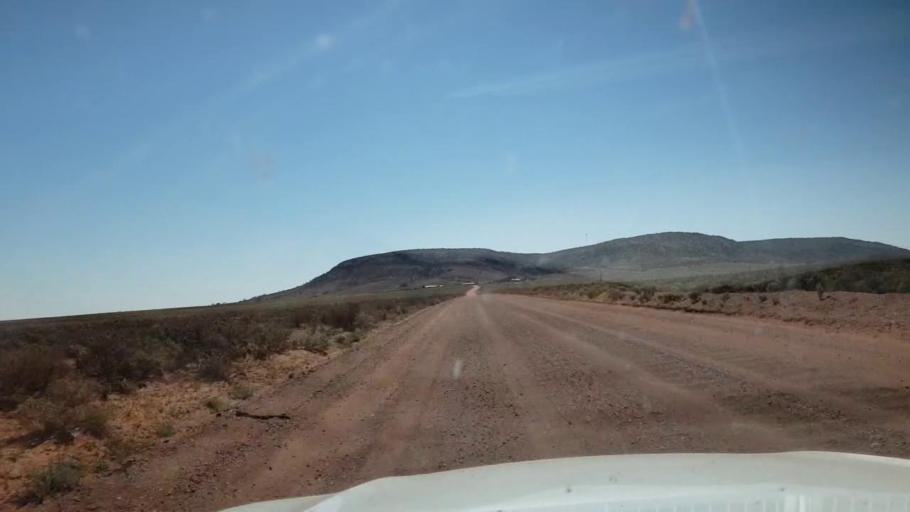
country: AU
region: South Australia
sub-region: Whyalla
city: Whyalla
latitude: -32.6975
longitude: 137.1325
